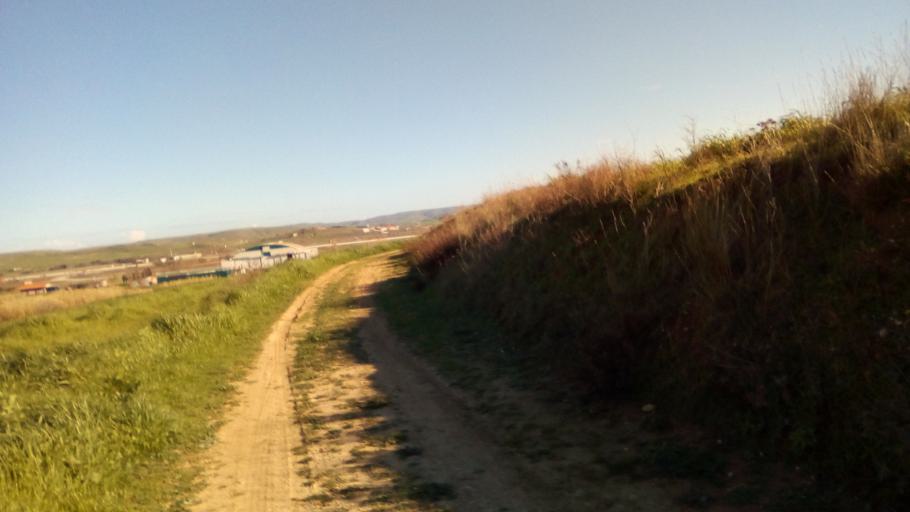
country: GR
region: North Aegean
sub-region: Nomos Lesvou
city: Myrina
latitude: 39.9320
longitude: 25.2361
